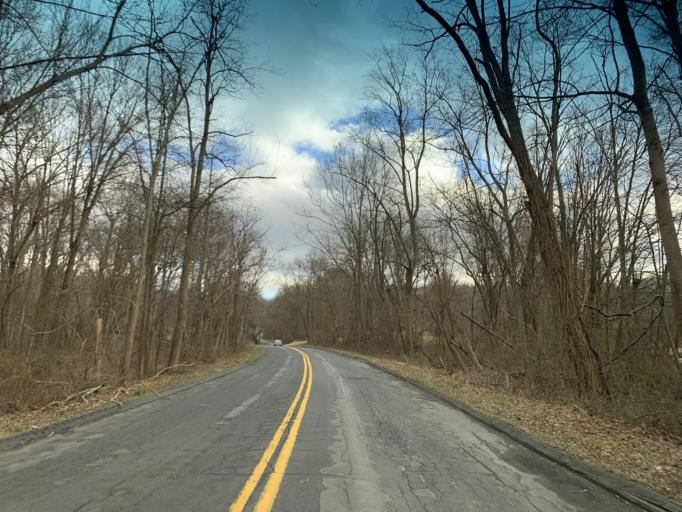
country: US
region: Maryland
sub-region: Harford County
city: Bel Air North
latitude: 39.6138
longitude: -76.3147
